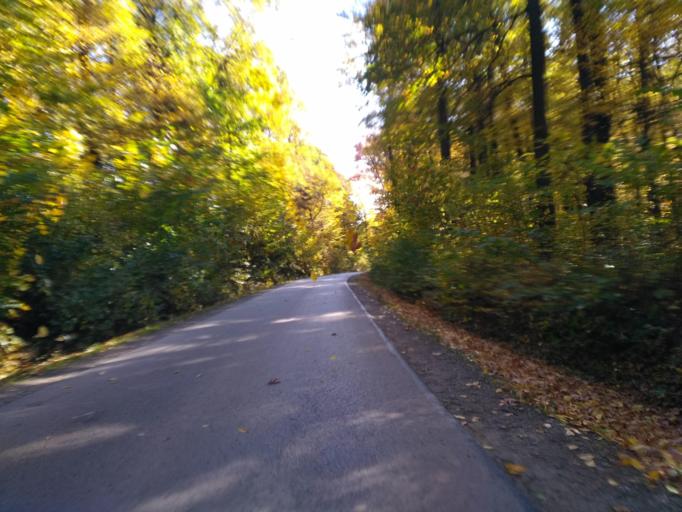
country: PL
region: Subcarpathian Voivodeship
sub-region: Powiat ropczycko-sedziszowski
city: Iwierzyce
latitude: 50.0467
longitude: 21.7729
